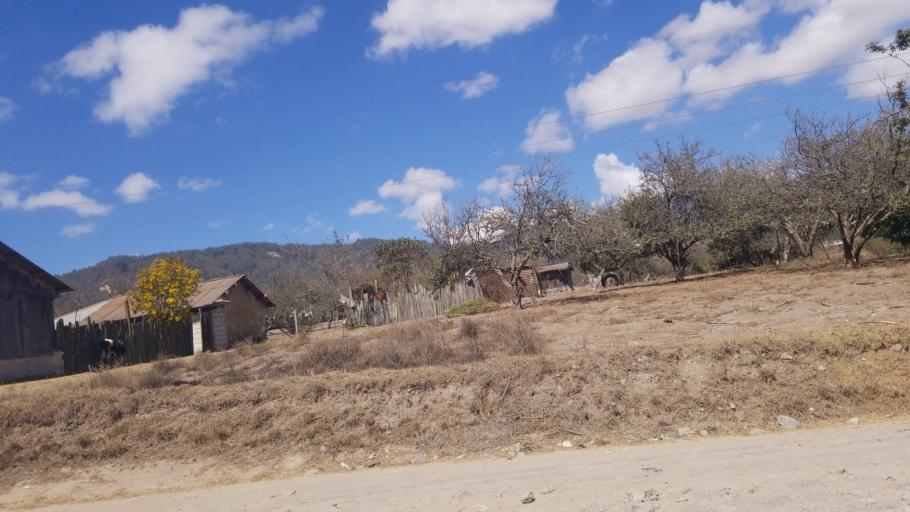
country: GT
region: Quetzaltenango
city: Almolonga
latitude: 14.7913
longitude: -91.5373
